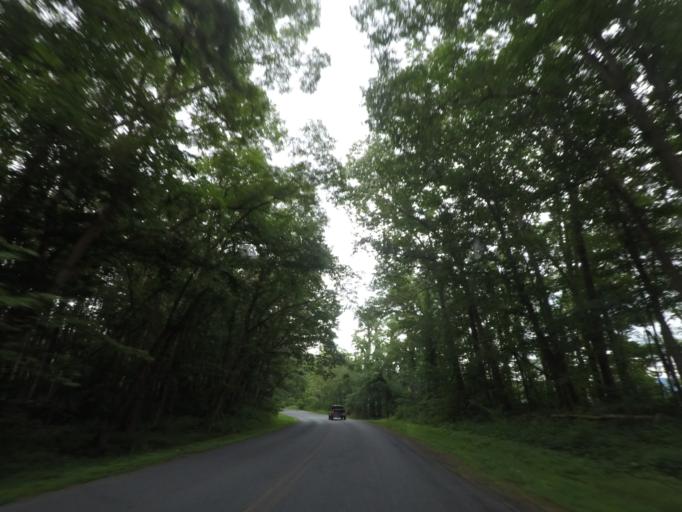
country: US
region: New York
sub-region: Rensselaer County
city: Poestenkill
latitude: 42.8393
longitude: -73.5297
